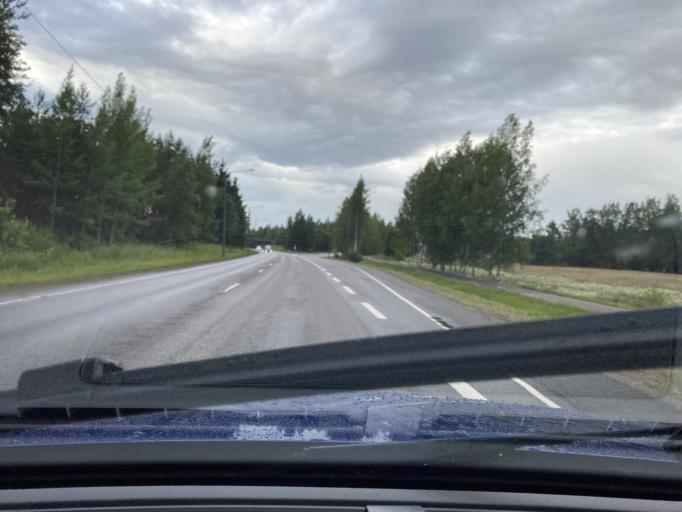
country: FI
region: Uusimaa
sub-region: Helsinki
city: Hyvinge
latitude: 60.6164
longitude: 24.8118
